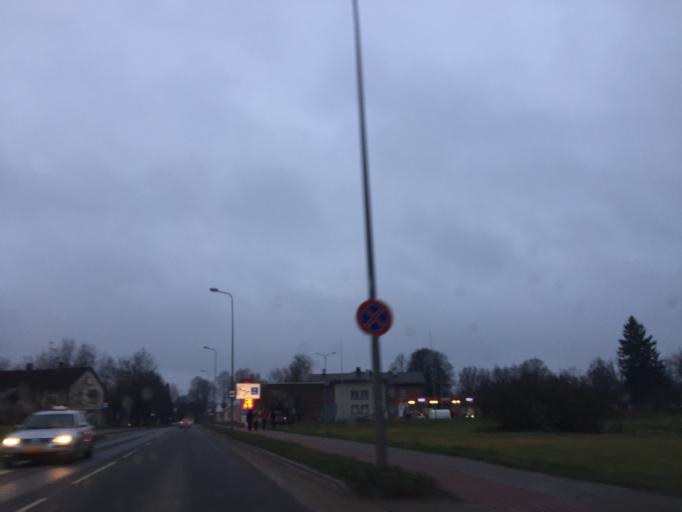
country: LV
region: Valmieras Rajons
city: Valmiera
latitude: 57.5378
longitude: 25.4032
